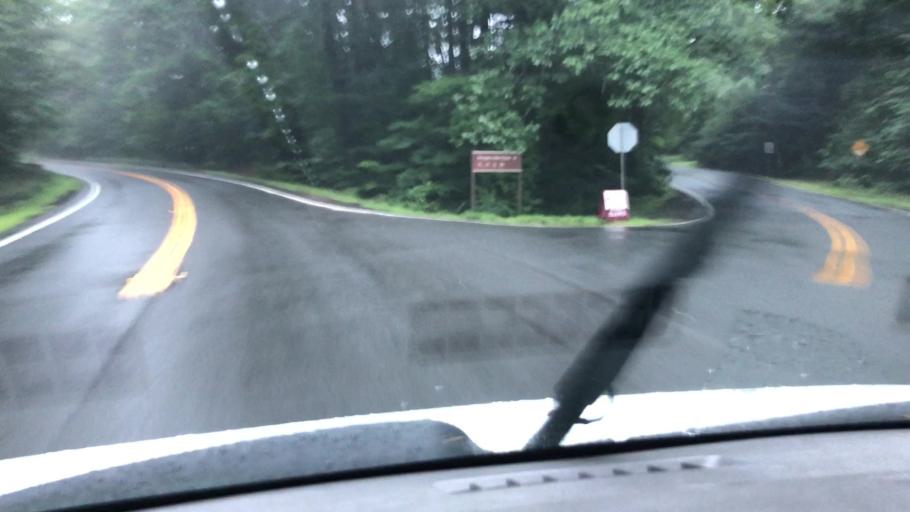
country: US
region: Massachusetts
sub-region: Hampshire County
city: Westhampton
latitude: 42.2811
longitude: -72.8665
